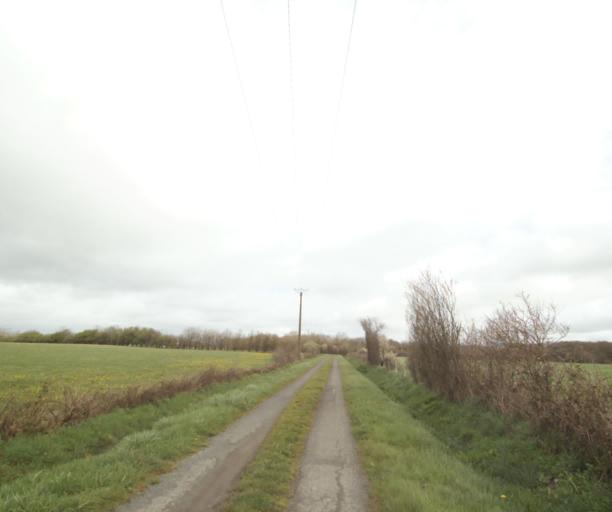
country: FR
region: Pays de la Loire
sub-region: Departement de la Loire-Atlantique
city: Bouvron
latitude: 47.4256
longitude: -1.8929
